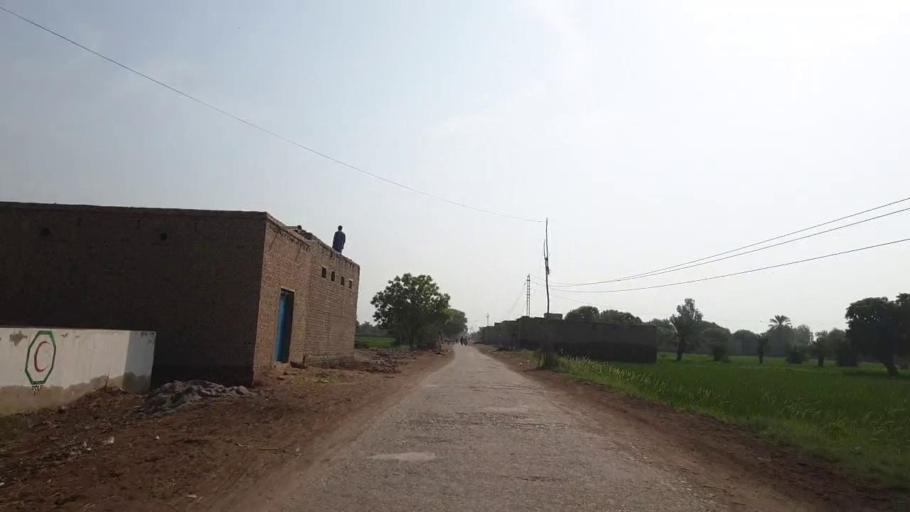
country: PK
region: Sindh
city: Larkana
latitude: 27.4575
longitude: 68.2090
